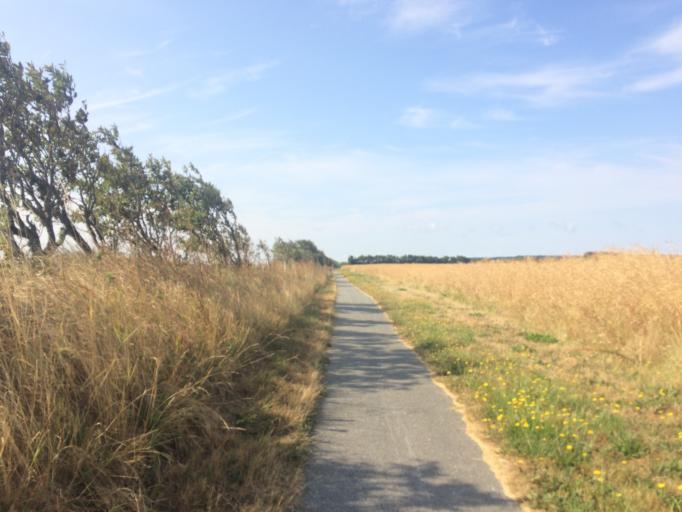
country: DK
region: Central Jutland
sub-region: Holstebro Kommune
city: Vinderup
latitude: 56.6353
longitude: 8.7875
